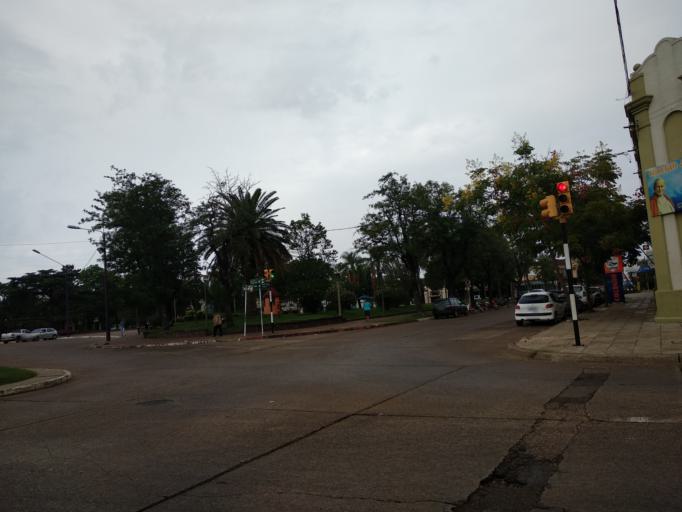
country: UY
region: Artigas
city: Artigas
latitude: -30.4045
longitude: -56.4696
